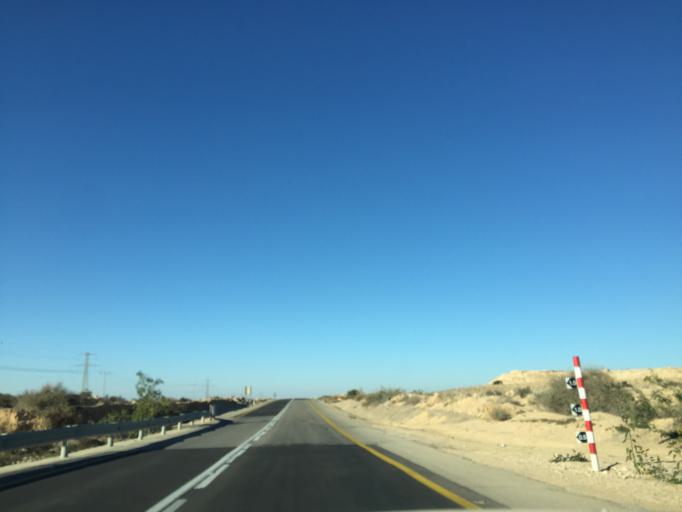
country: IL
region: Southern District
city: Midreshet Ben-Gurion
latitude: 30.7797
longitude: 34.7692
